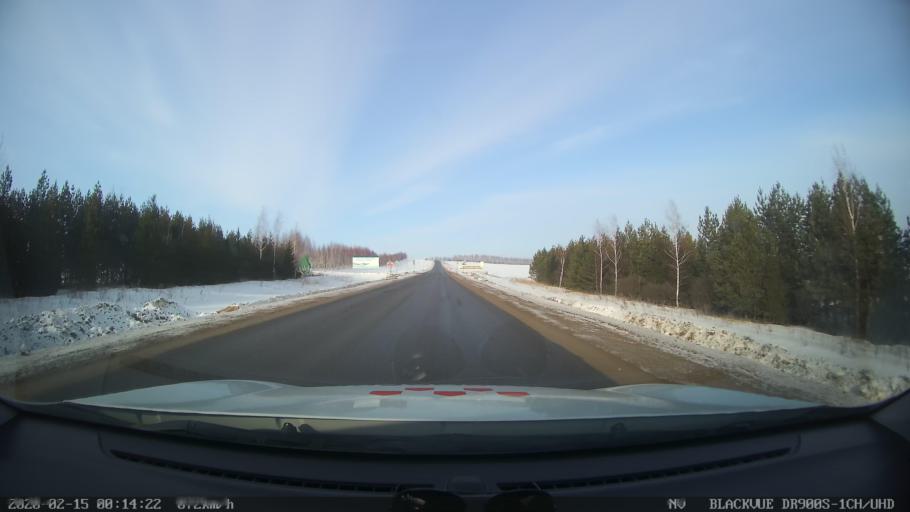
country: RU
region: Tatarstan
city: Stolbishchi
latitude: 55.4851
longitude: 49.0044
